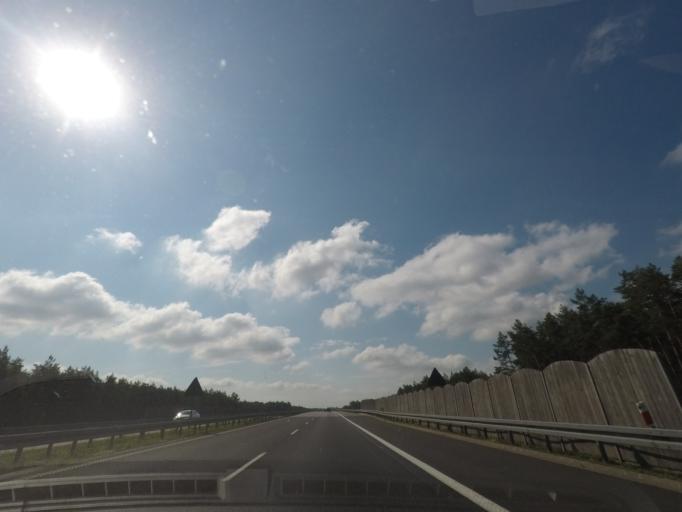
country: PL
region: Kujawsko-Pomorskie
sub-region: Powiat swiecki
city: Warlubie
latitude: 53.5081
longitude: 18.6084
